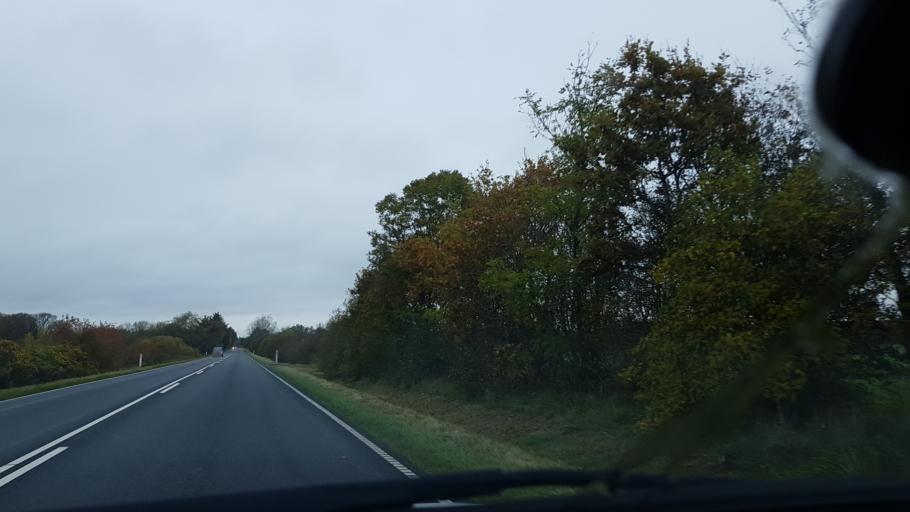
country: DK
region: South Denmark
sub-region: Esbjerg Kommune
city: Ribe
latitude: 55.2941
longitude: 8.8171
